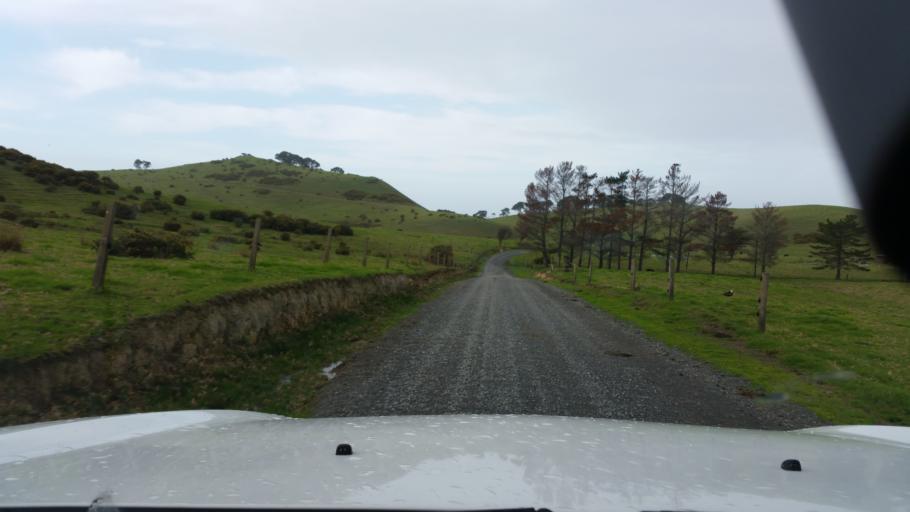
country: NZ
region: Northland
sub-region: Whangarei
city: Ruakaka
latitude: -35.7806
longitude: 174.5467
